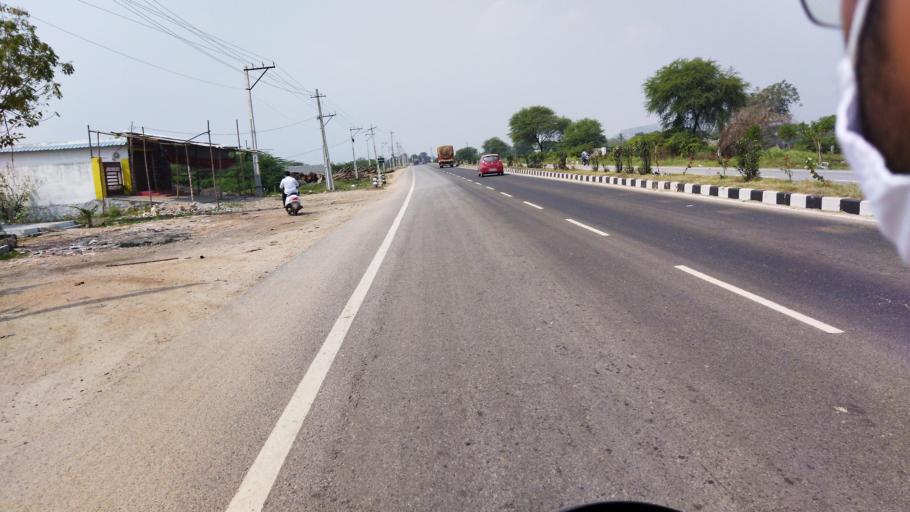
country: IN
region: Telangana
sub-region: Nalgonda
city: Nalgonda
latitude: 17.0759
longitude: 79.2828
